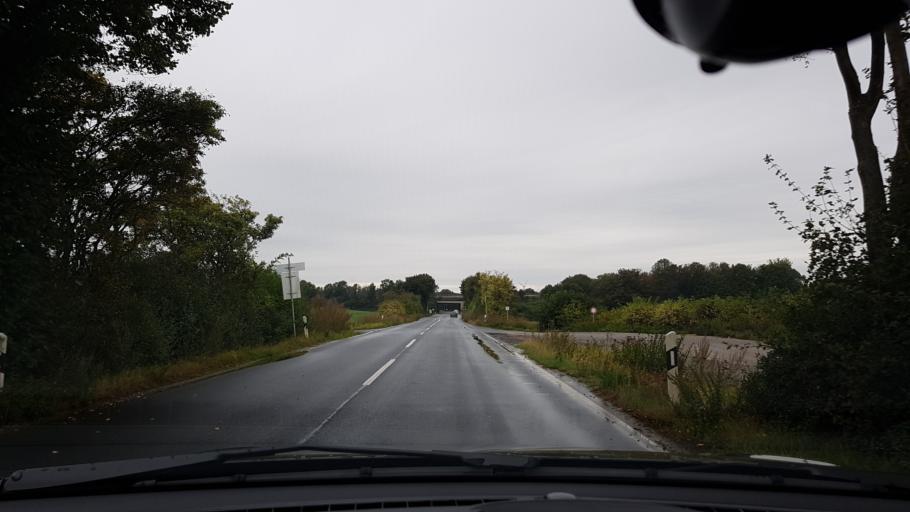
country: DE
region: North Rhine-Westphalia
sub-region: Regierungsbezirk Koln
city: Titz
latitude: 51.0434
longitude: 6.4599
